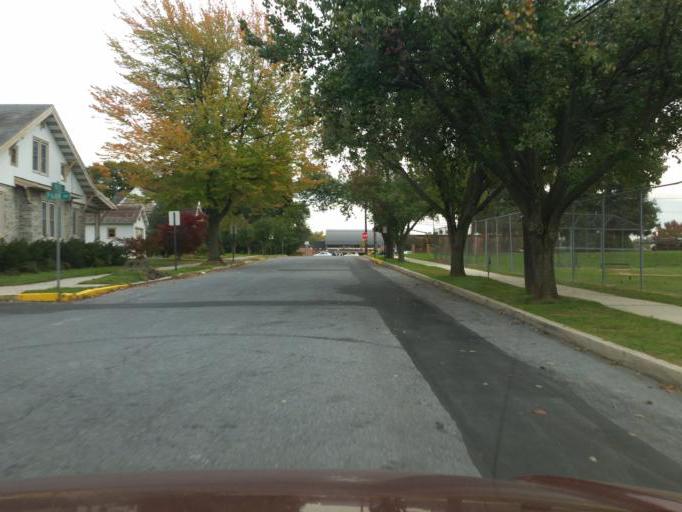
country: US
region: Pennsylvania
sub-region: Dauphin County
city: Hummelstown
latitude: 40.2622
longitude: -76.7056
